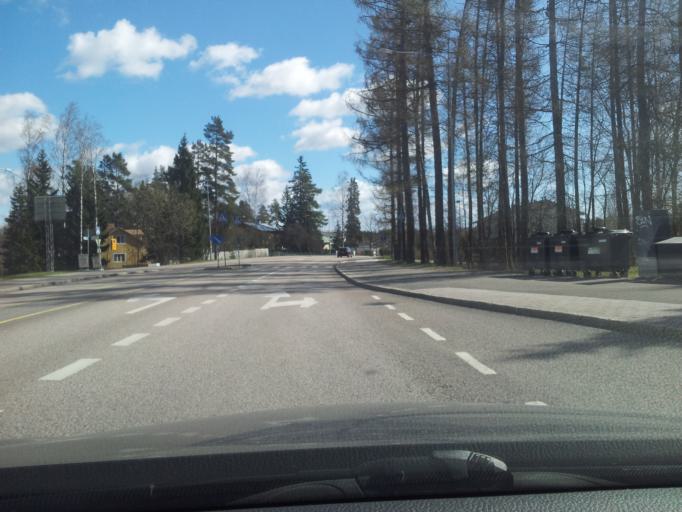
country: FI
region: Uusimaa
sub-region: Helsinki
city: Espoo
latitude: 60.1799
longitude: 24.6775
